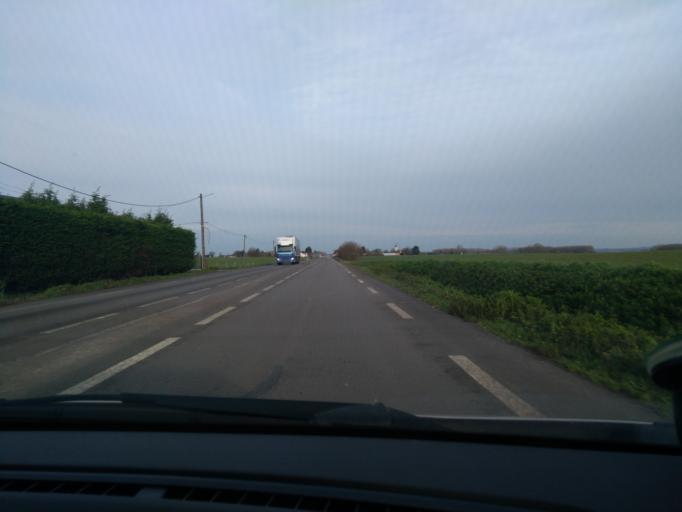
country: FR
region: Nord-Pas-de-Calais
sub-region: Departement du Nord
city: Maubeuge
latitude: 50.3255
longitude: 3.9751
